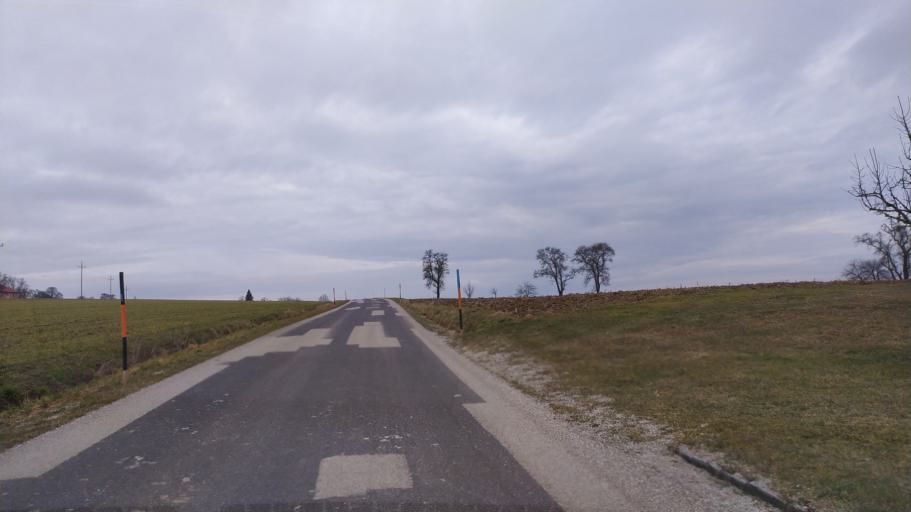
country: AT
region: Lower Austria
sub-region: Politischer Bezirk Amstetten
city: Zeillern
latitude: 48.1334
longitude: 14.7186
